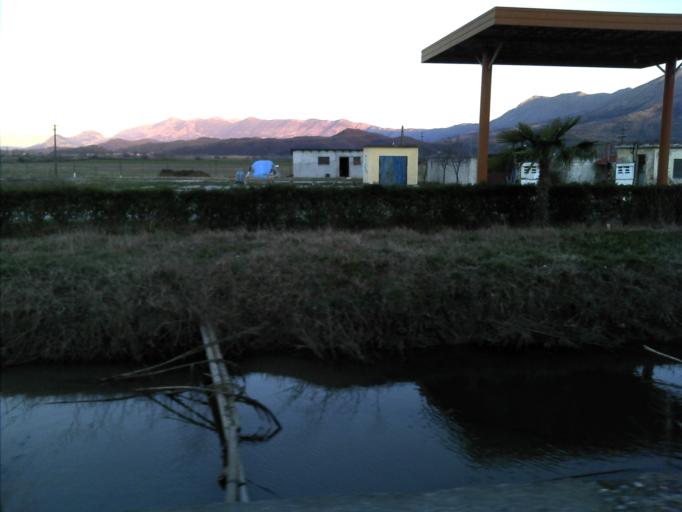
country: AL
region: Shkoder
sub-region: Rrethi i Shkodres
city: Berdica e Madhe
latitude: 42.0118
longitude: 19.4807
